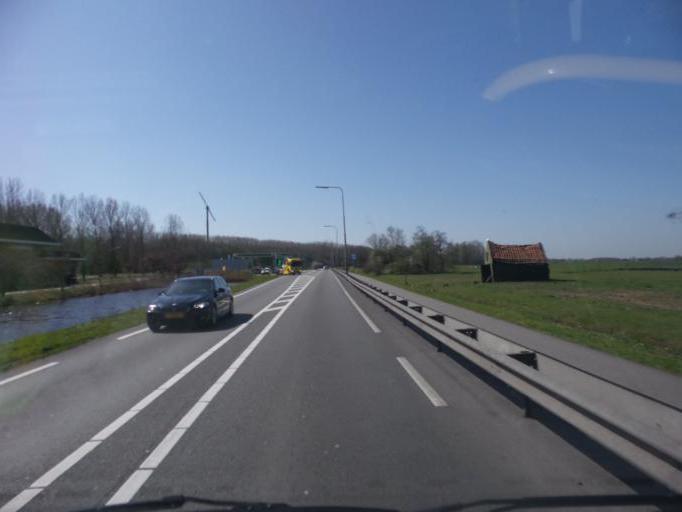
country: NL
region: South Holland
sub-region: Bodegraven-Reeuwijk
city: Bodegraven
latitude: 52.0673
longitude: 4.7385
